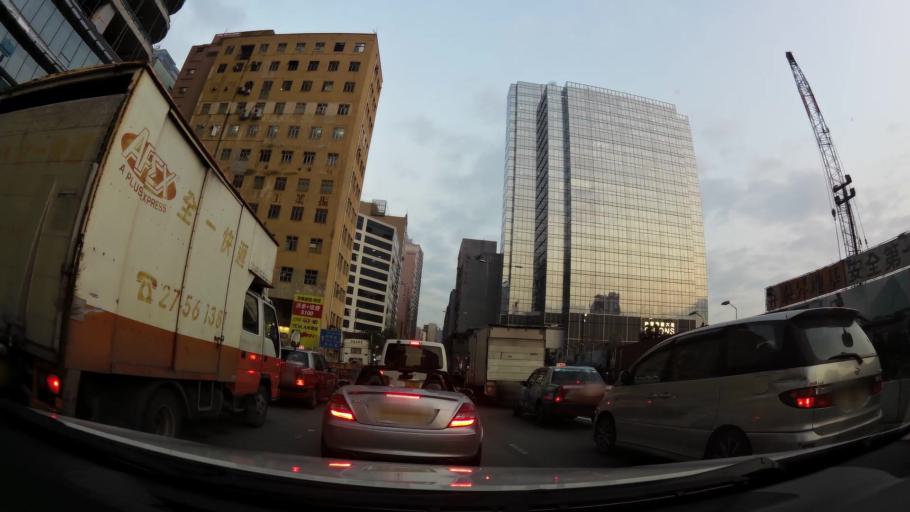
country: HK
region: Kowloon City
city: Kowloon
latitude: 22.3146
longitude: 114.2166
